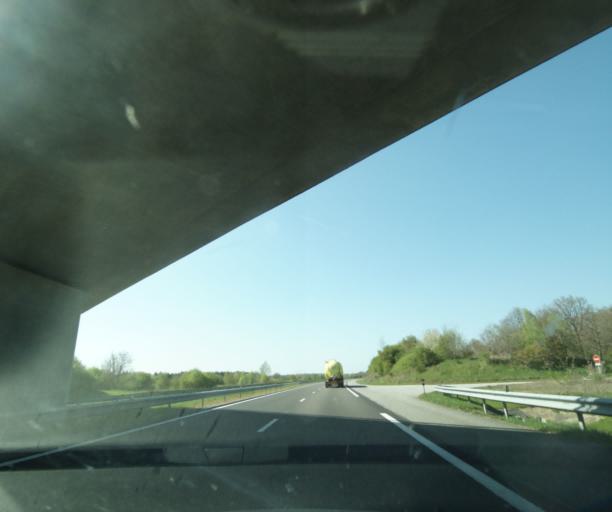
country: FR
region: Centre
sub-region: Departement du Loiret
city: Ouzouer-sur-Trezee
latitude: 47.6208
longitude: 2.8003
